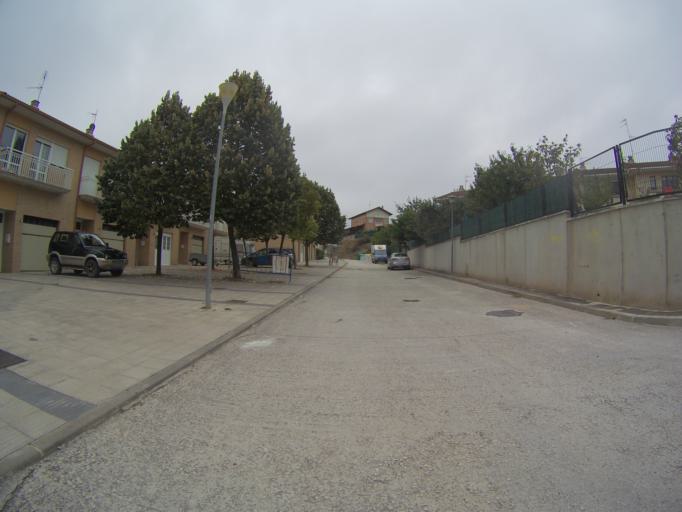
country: ES
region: Navarre
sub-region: Provincia de Navarra
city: Ayegui
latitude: 42.6599
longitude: -2.0369
